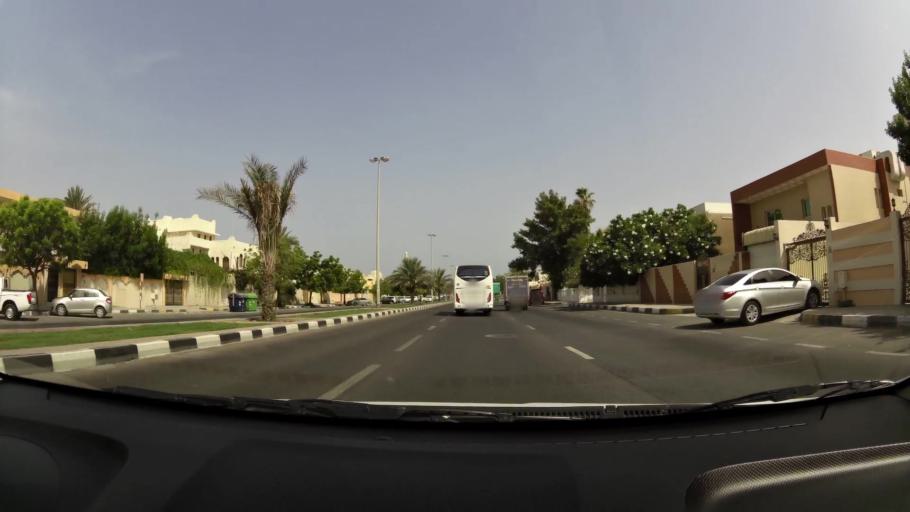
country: AE
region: Ash Shariqah
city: Sharjah
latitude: 25.3666
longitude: 55.4174
